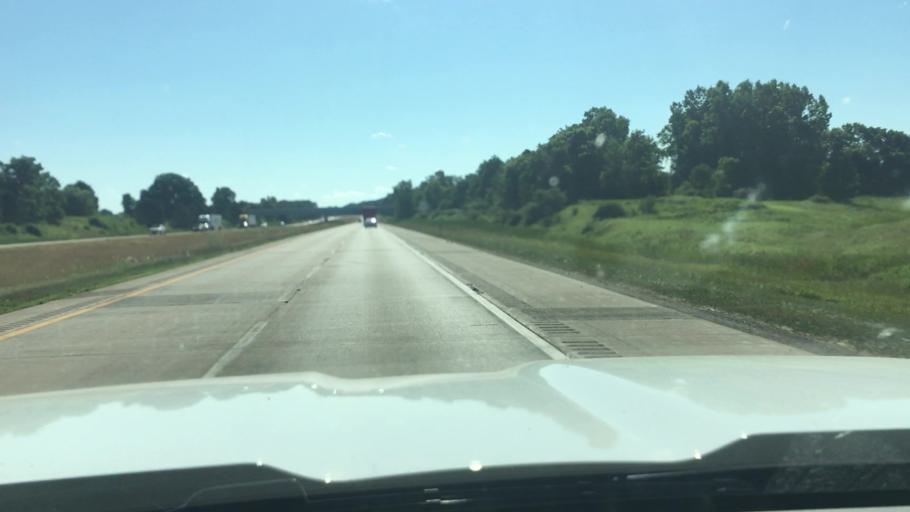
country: US
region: Michigan
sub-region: Clinton County
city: DeWitt
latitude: 42.8074
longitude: -84.6080
